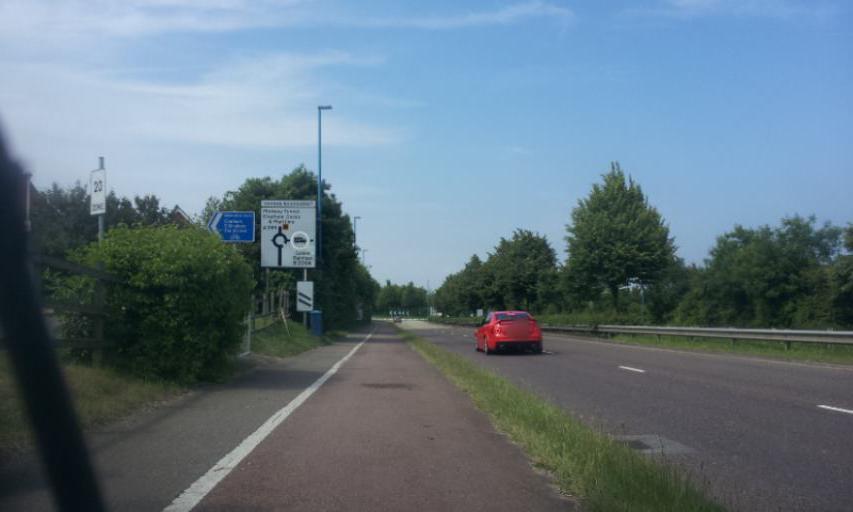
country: GB
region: England
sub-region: Kent
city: Gillingham
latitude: 51.3866
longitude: 0.5781
